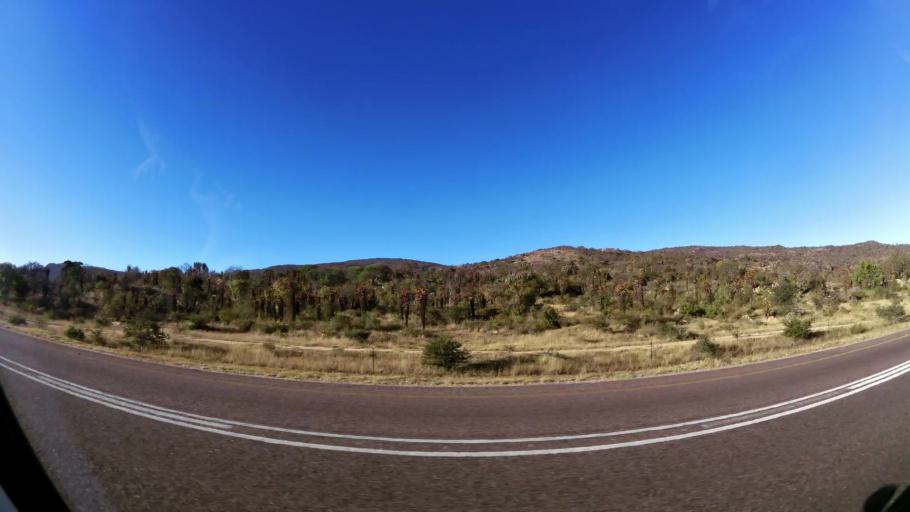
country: ZA
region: Limpopo
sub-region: Capricorn District Municipality
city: Mankoeng
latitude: -23.9334
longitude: 29.8411
